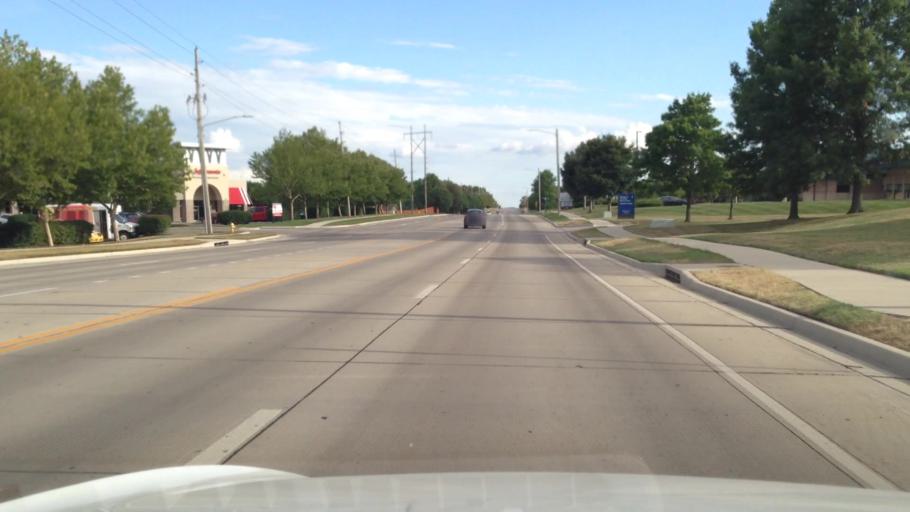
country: US
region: Kansas
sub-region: Douglas County
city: Lawrence
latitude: 38.9564
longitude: -95.3071
